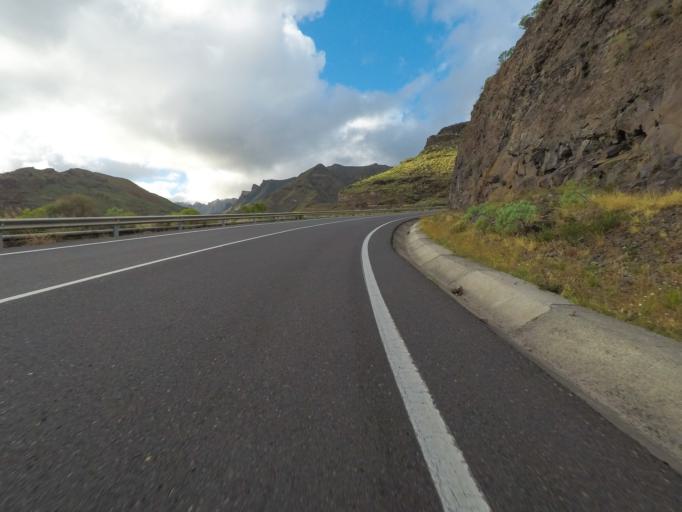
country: ES
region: Canary Islands
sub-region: Provincia de Santa Cruz de Tenerife
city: San Sebastian de la Gomera
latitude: 28.1150
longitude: -17.1383
